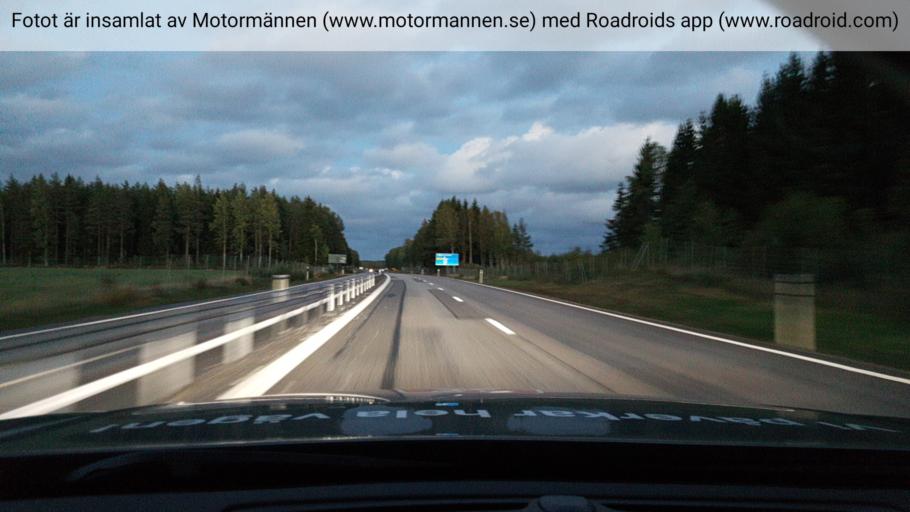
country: SE
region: Vaermland
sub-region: Kristinehamns Kommun
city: Kristinehamn
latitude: 59.3808
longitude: 13.8907
